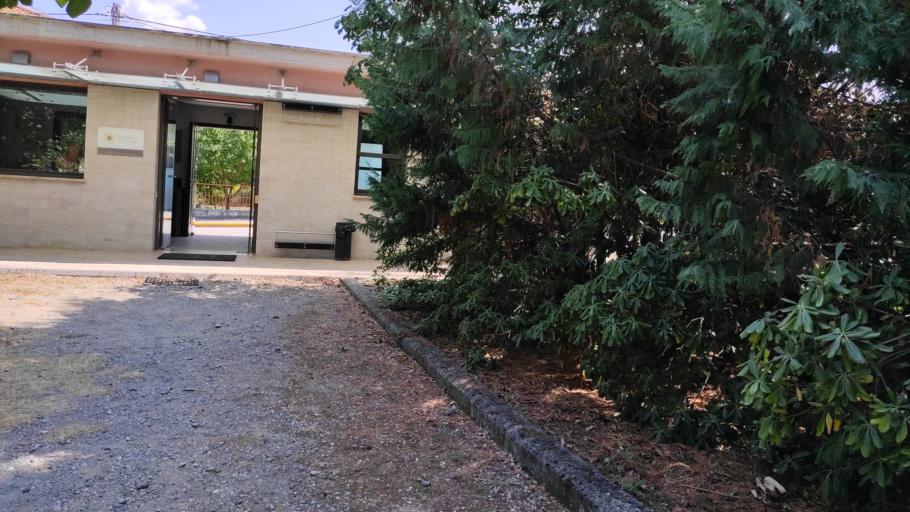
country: GR
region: Central Macedonia
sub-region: Nomos Imathias
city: Vergina
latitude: 40.4868
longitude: 22.3205
